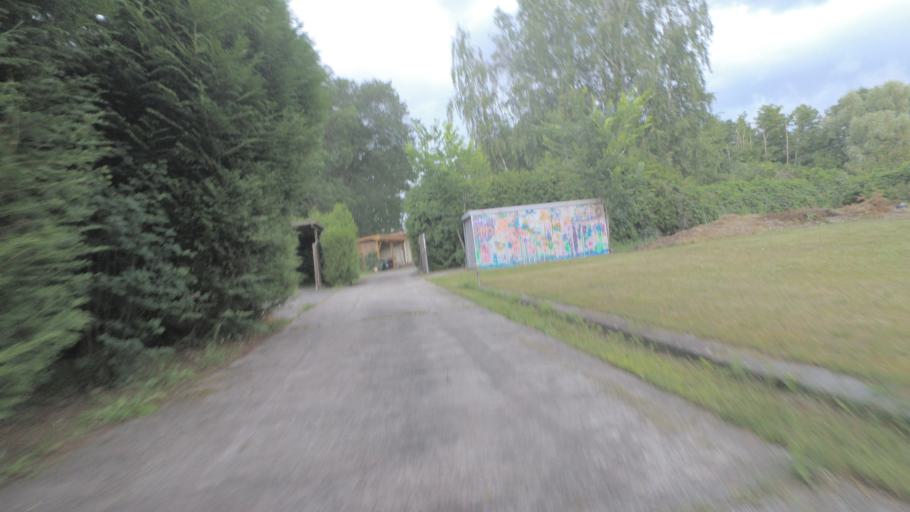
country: DE
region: Brandenburg
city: Bestensee
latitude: 52.2266
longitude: 13.6532
